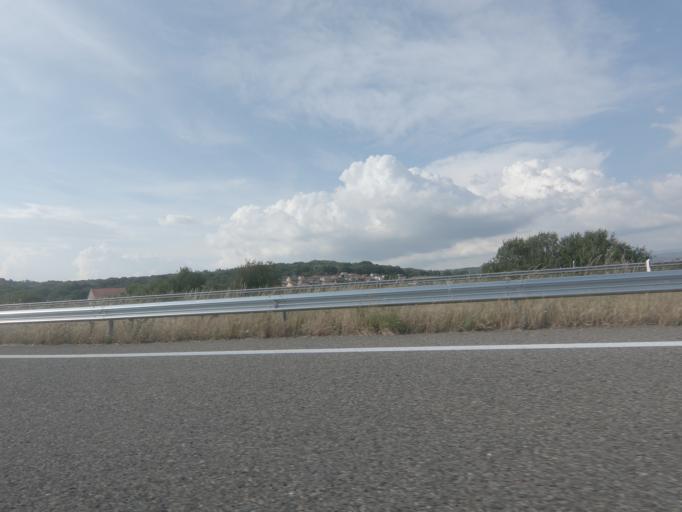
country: ES
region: Galicia
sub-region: Provincia de Ourense
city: Xinzo de Limia
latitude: 42.0633
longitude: -7.6832
